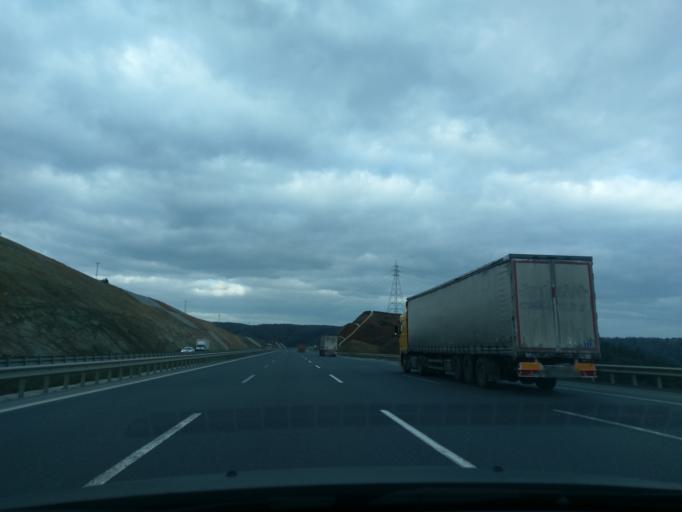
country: TR
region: Istanbul
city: Basaksehir
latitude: 41.1619
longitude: 28.8102
